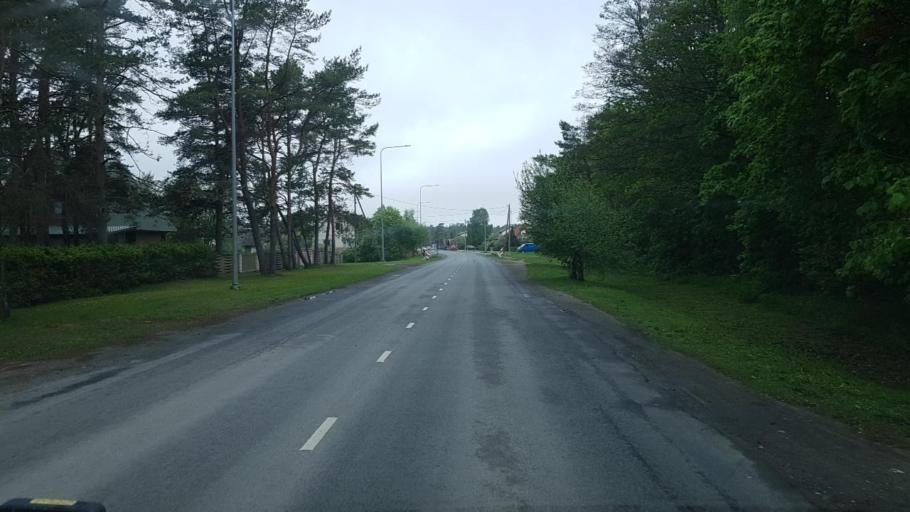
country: EE
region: Laeaene
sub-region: Haapsalu linn
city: Haapsalu
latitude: 58.9291
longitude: 23.5343
